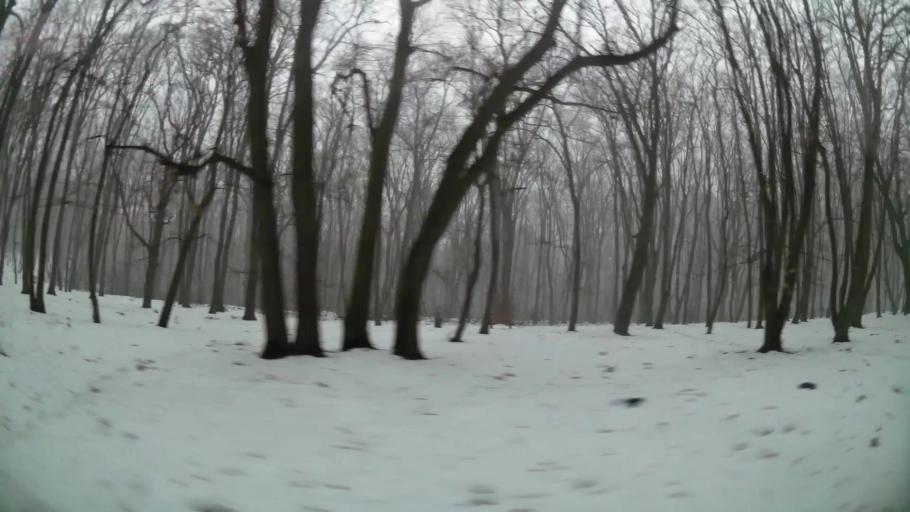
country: RS
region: Central Serbia
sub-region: Belgrade
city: Cukarica
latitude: 44.7734
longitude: 20.4254
